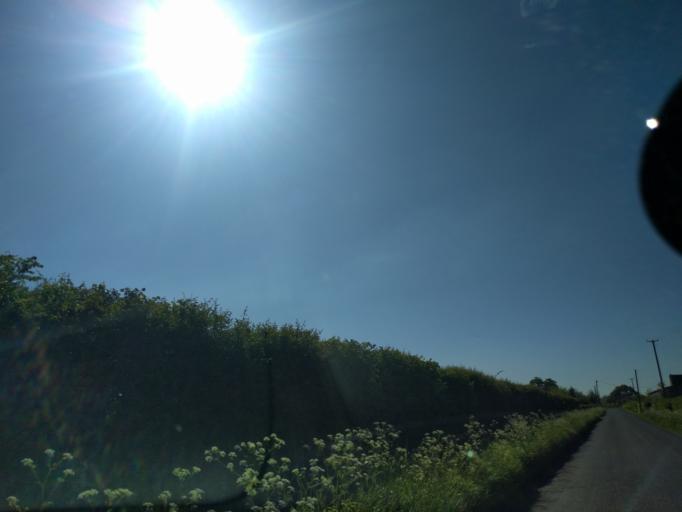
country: GB
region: England
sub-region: Wiltshire
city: Bratton
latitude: 51.2930
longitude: -2.1315
